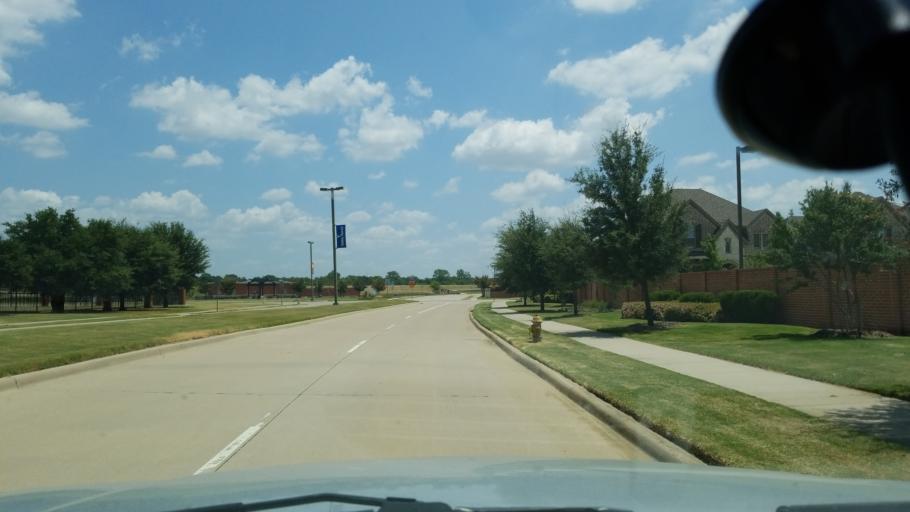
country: US
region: Texas
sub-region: Dallas County
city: Farmers Branch
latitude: 32.9166
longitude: -96.9452
